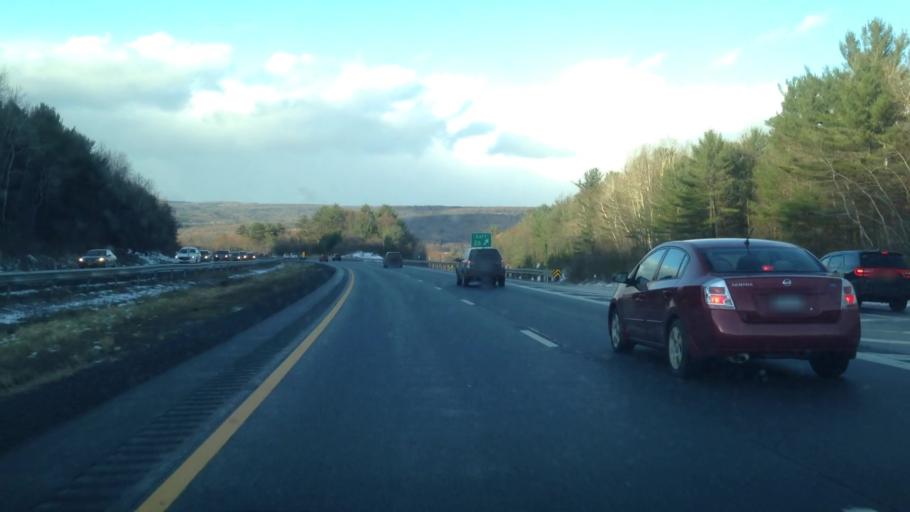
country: US
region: New York
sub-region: Schenectady County
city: Scotia
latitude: 42.8318
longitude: -74.0110
